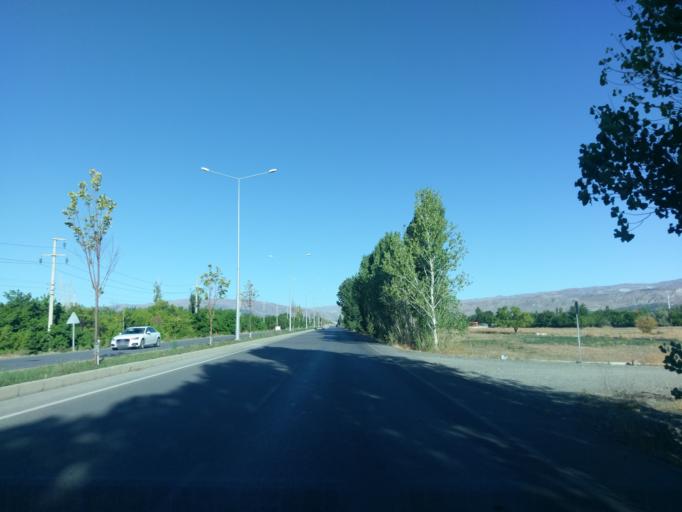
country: TR
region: Erzincan
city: Erzincan
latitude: 39.7699
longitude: 39.4270
